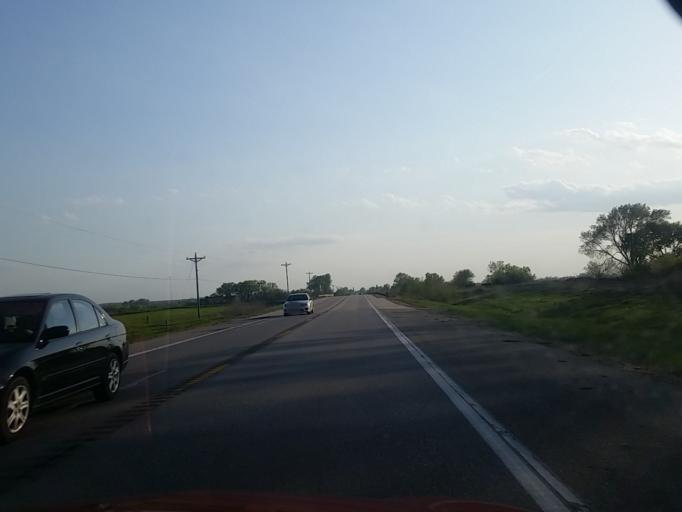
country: US
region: Nebraska
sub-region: Sarpy County
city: Gretna
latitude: 41.0803
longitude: -96.2942
